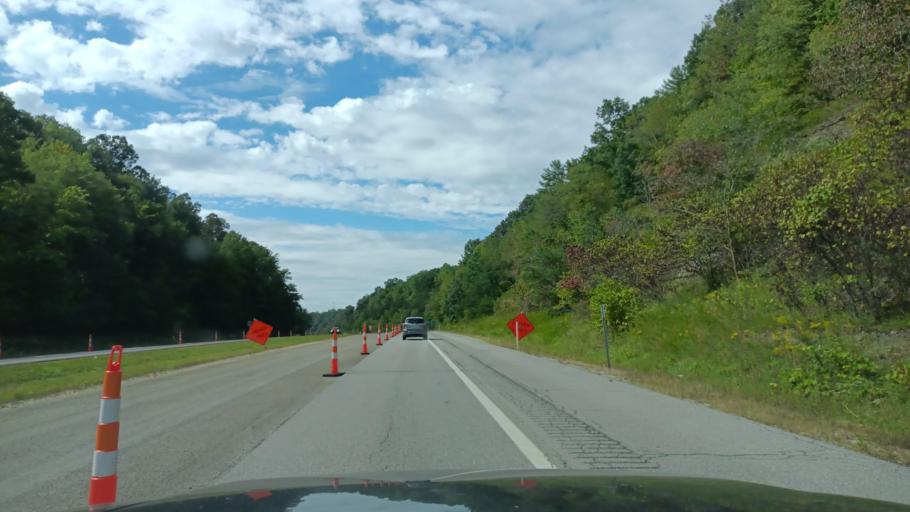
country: US
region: West Virginia
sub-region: Ritchie County
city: Harrisville
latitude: 39.2612
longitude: -81.0888
